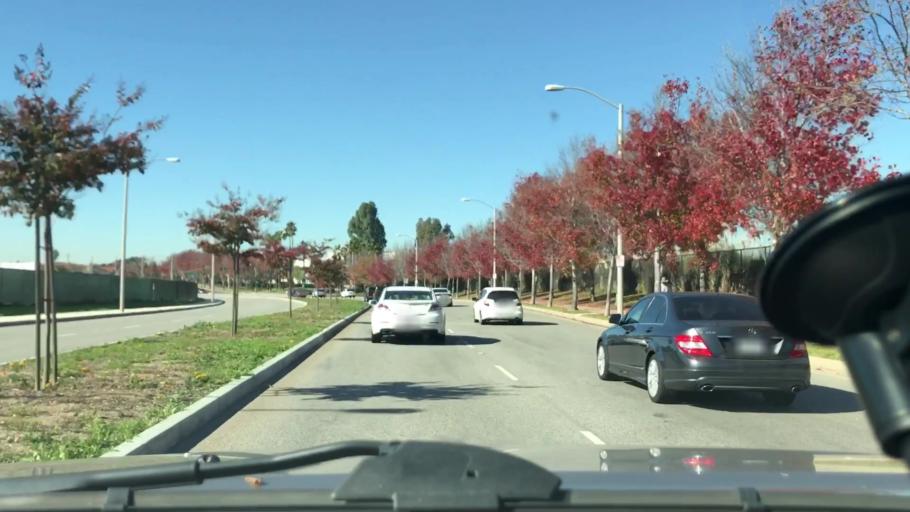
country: US
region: California
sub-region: Los Angeles County
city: Torrance
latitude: 33.8482
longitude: -118.3428
